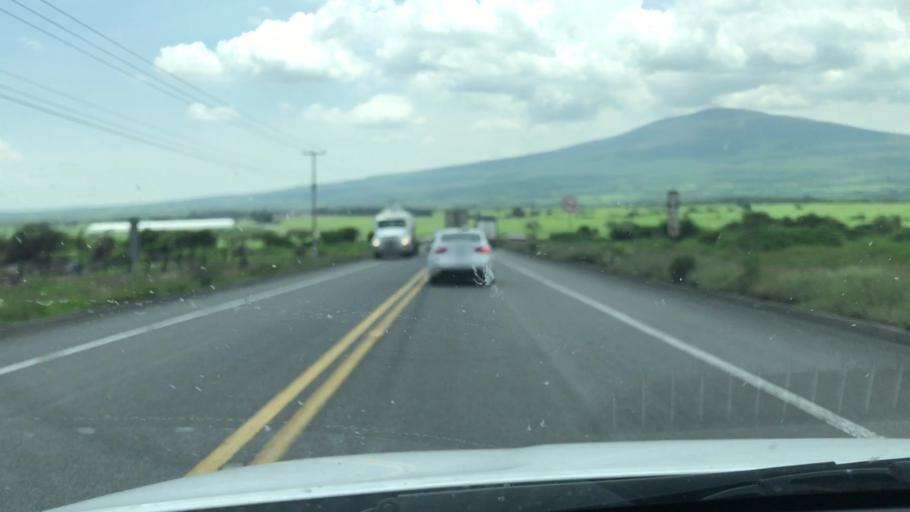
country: MX
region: Michoacan
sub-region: Yurecuaro
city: Yurecuaro
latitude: 20.3384
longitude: -102.1940
